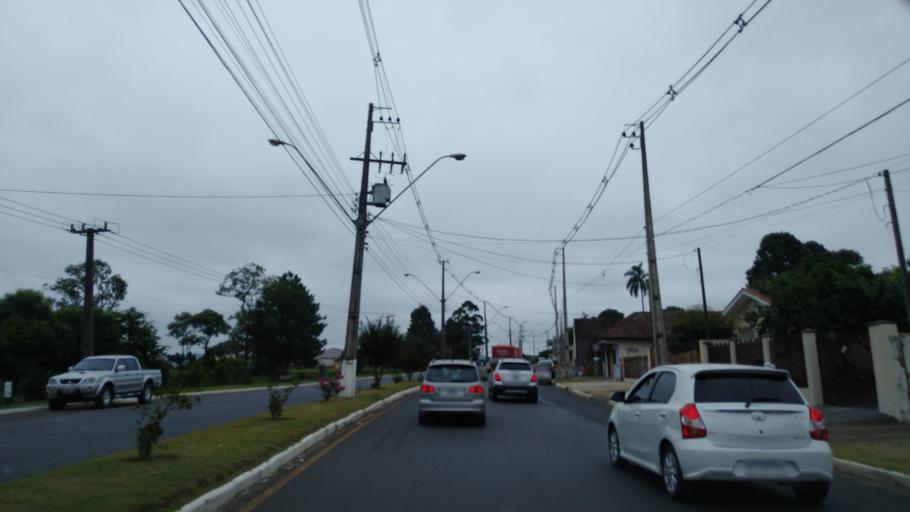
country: BR
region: Santa Catarina
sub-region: Porto Uniao
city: Porto Uniao
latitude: -26.2533
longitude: -51.0799
